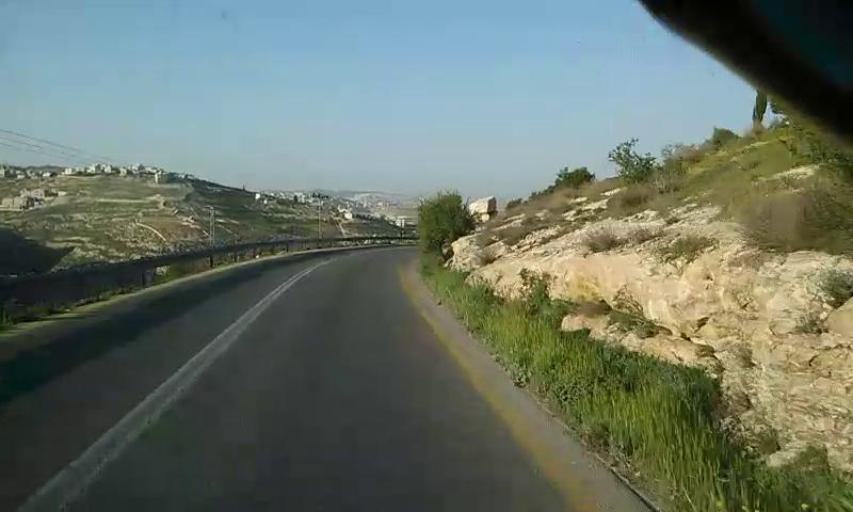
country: PS
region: West Bank
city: Marah Rabbah
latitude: 31.6494
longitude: 35.2042
